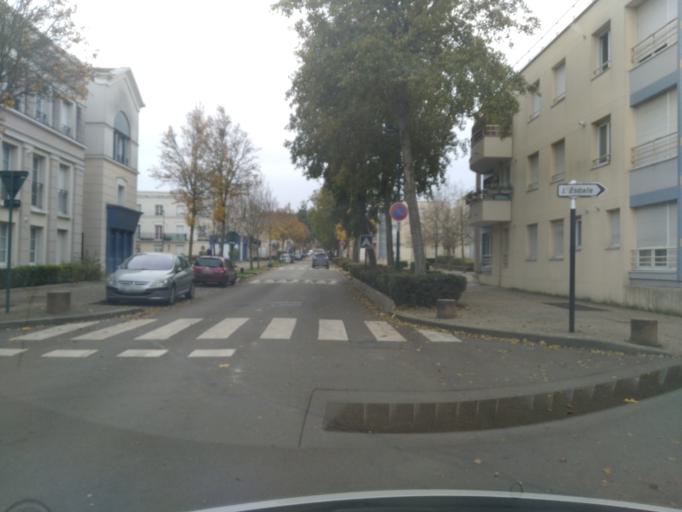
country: FR
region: Ile-de-France
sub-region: Departement des Yvelines
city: Plaisir
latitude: 48.8205
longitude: 1.9658
